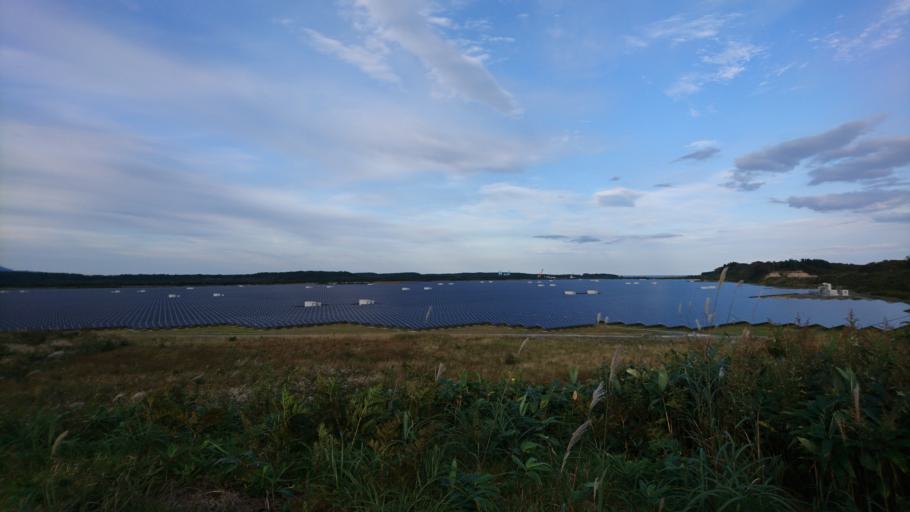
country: JP
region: Aomori
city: Misawa
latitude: 40.9229
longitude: 141.3553
